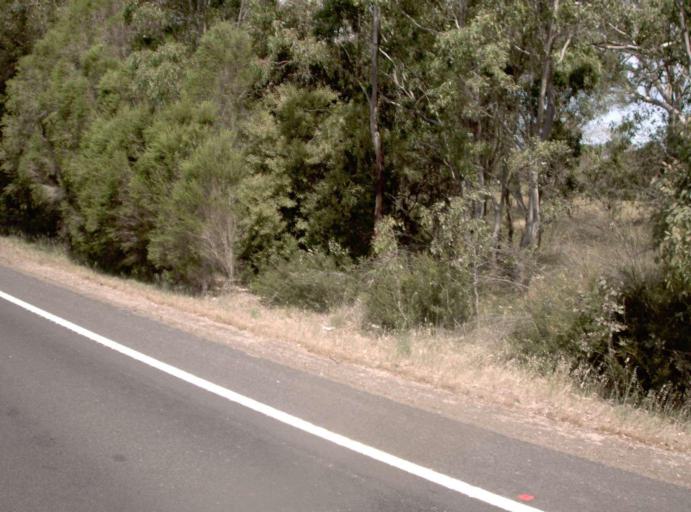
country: AU
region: Victoria
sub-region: Wellington
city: Sale
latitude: -37.9264
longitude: 147.2209
